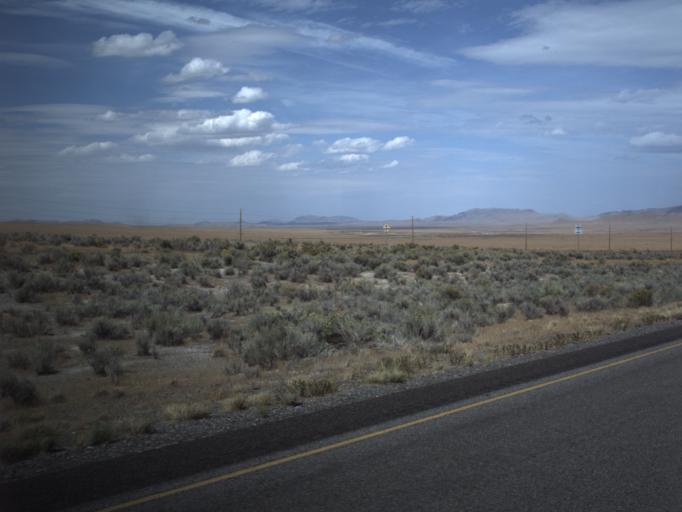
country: US
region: Utah
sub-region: Tooele County
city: Grantsville
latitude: 40.7694
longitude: -112.9825
